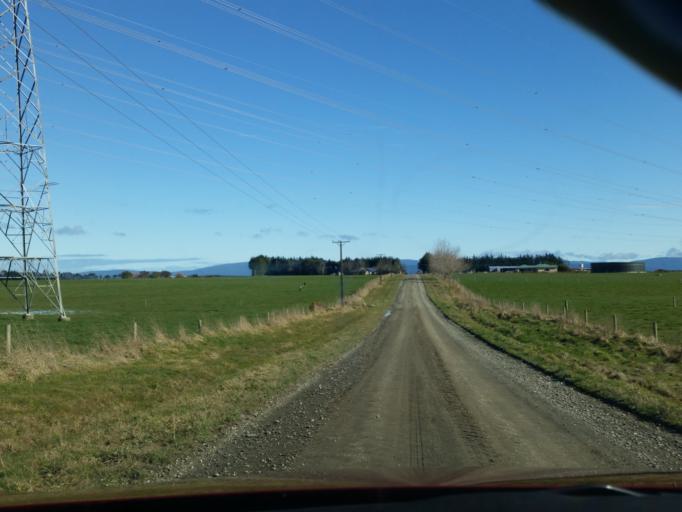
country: NZ
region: Southland
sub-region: Southland District
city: Winton
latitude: -46.2055
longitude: 168.2038
